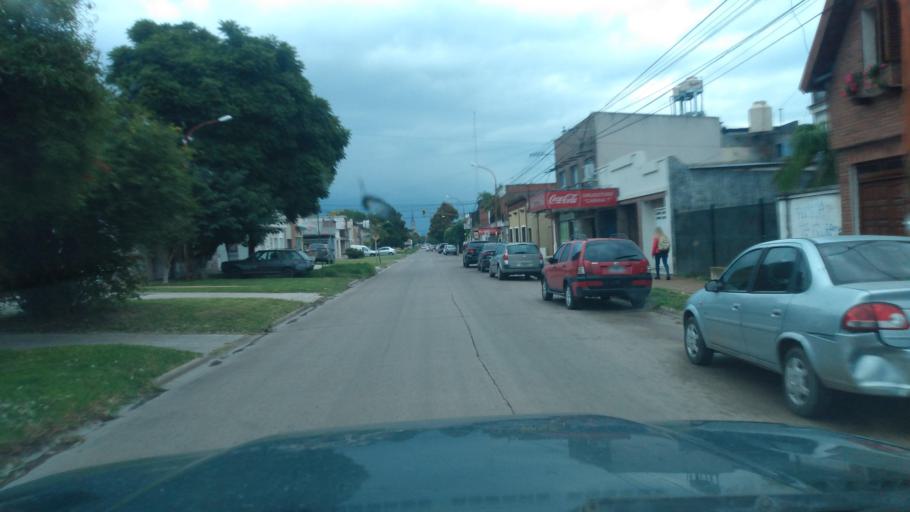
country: AR
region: Buenos Aires
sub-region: Partido de Lujan
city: Lujan
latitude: -34.5697
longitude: -59.1016
